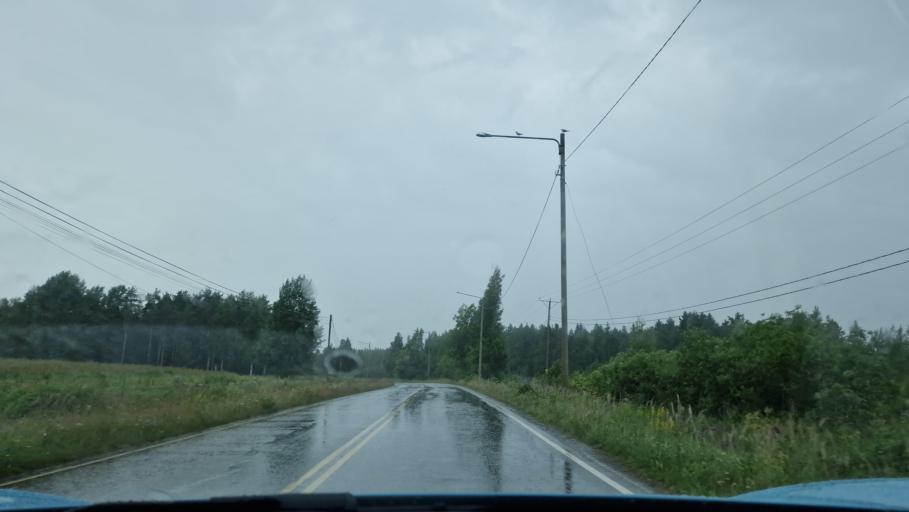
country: FI
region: Southern Ostrobothnia
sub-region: Jaerviseutu
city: Soini
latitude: 62.8431
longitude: 24.3271
